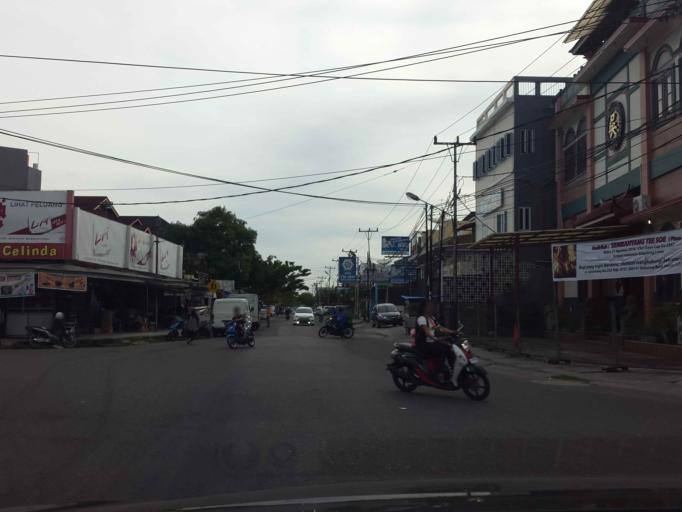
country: ID
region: West Sumatra
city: Padang
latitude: -0.9591
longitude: 100.3608
